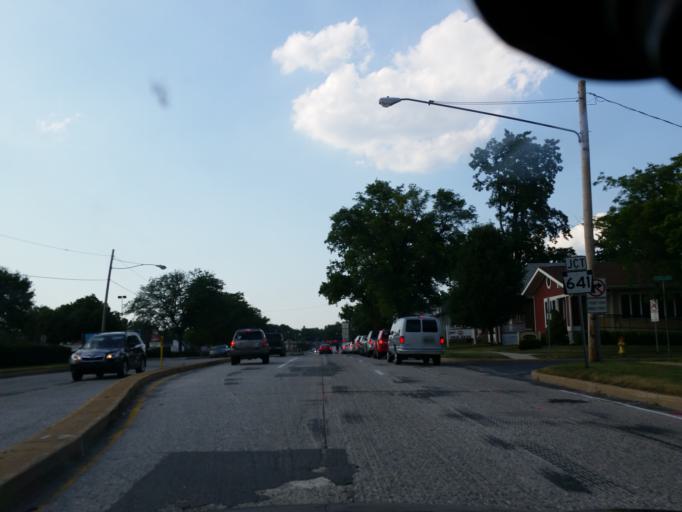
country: US
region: Pennsylvania
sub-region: Cumberland County
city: Camp Hill
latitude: 40.2359
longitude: -76.9335
